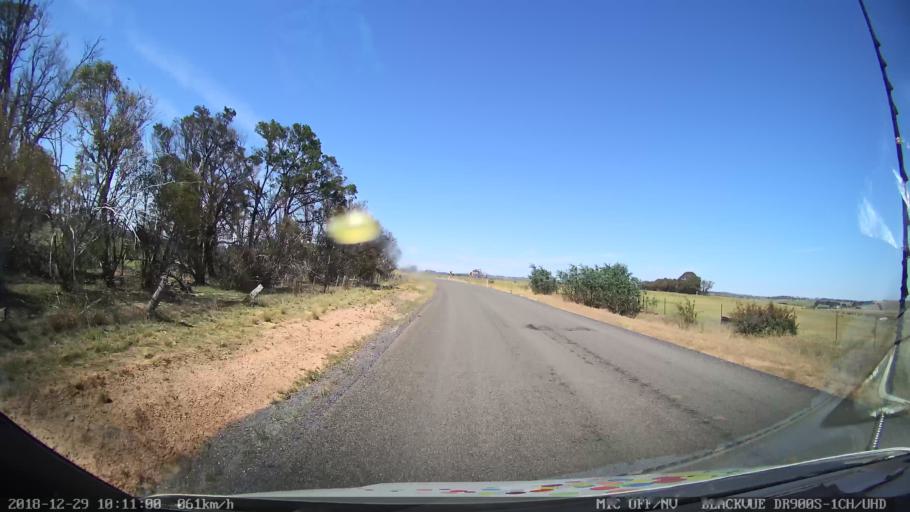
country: AU
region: New South Wales
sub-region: Yass Valley
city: Gundaroo
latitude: -34.8796
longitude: 149.4536
